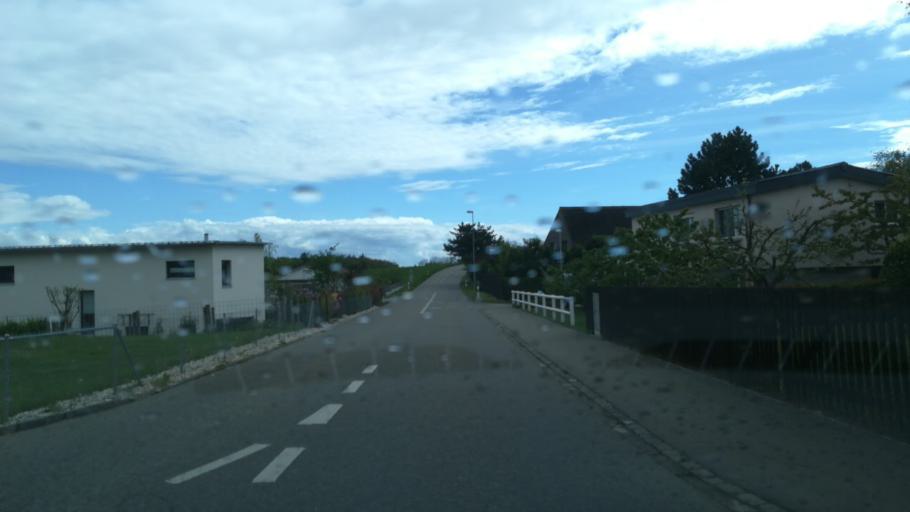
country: CH
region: Schaffhausen
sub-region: Bezirk Reiat
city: Stetten
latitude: 47.7537
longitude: 8.6682
